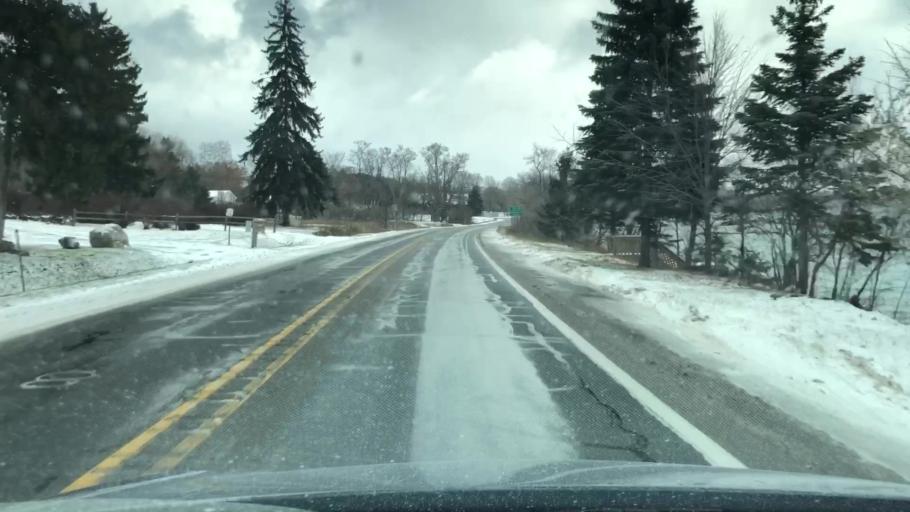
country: US
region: Michigan
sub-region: Grand Traverse County
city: Traverse City
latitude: 44.8158
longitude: -85.5579
